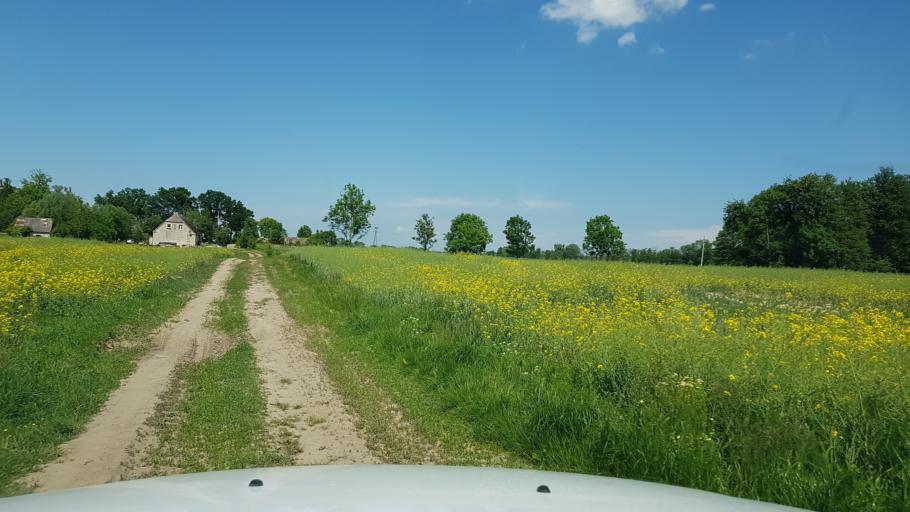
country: PL
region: West Pomeranian Voivodeship
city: Trzcinsko Zdroj
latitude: 52.9417
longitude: 14.5805
